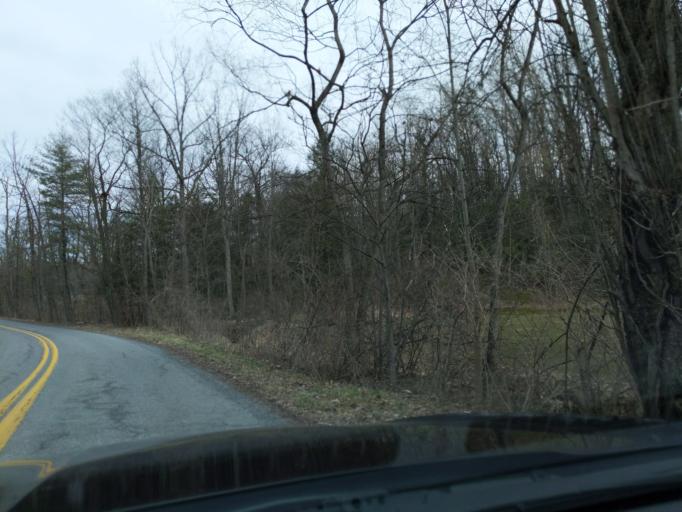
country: US
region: Pennsylvania
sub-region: Blair County
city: Greenwood
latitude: 40.5800
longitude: -78.3803
